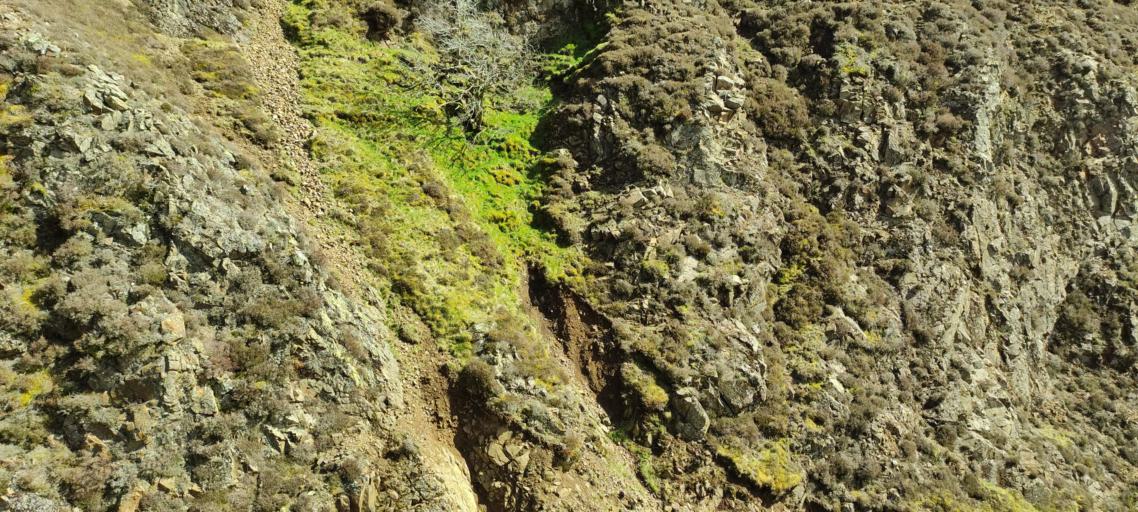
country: GB
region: England
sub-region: Cumbria
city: Keswick
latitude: 54.6907
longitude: -3.0520
